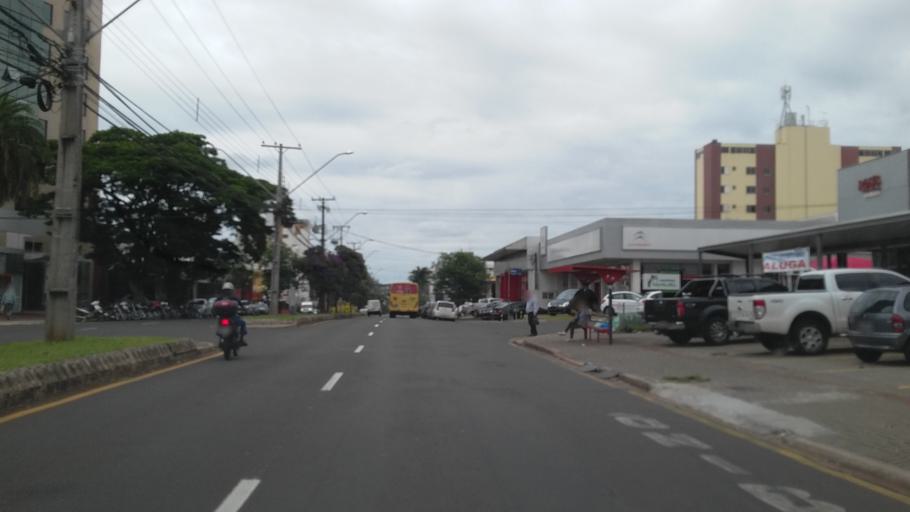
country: BR
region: Parana
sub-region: Londrina
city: Londrina
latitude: -23.3235
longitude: -51.1677
